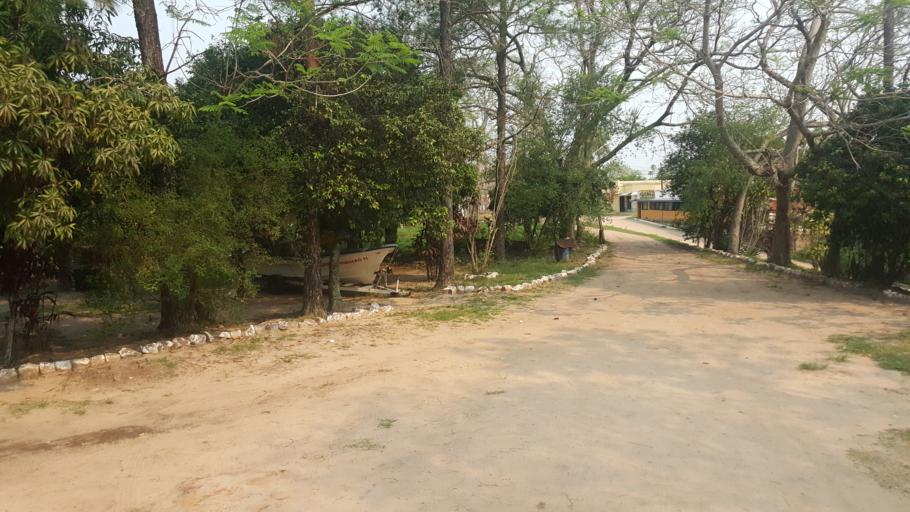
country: AR
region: Corrientes
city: Ita Ibate
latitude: -27.4237
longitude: -57.3382
